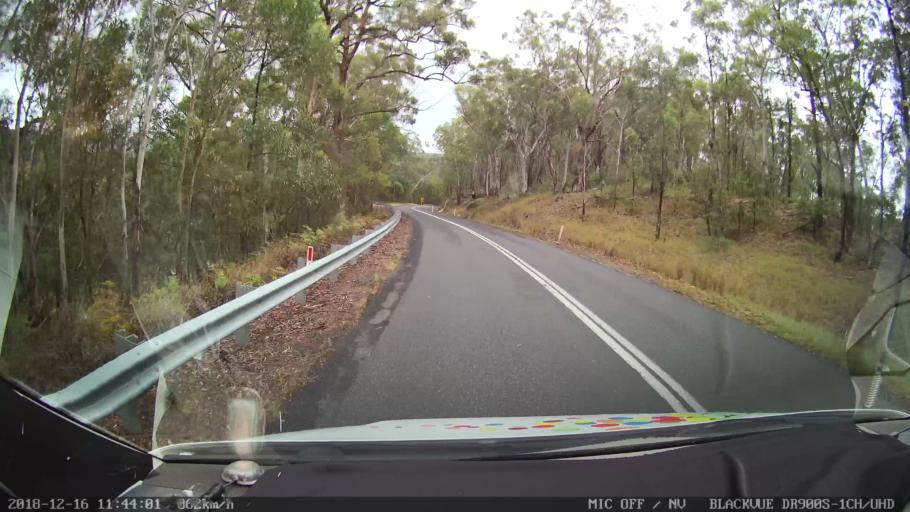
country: AU
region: New South Wales
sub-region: Tenterfield Municipality
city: Carrolls Creek
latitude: -28.9419
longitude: 152.2206
